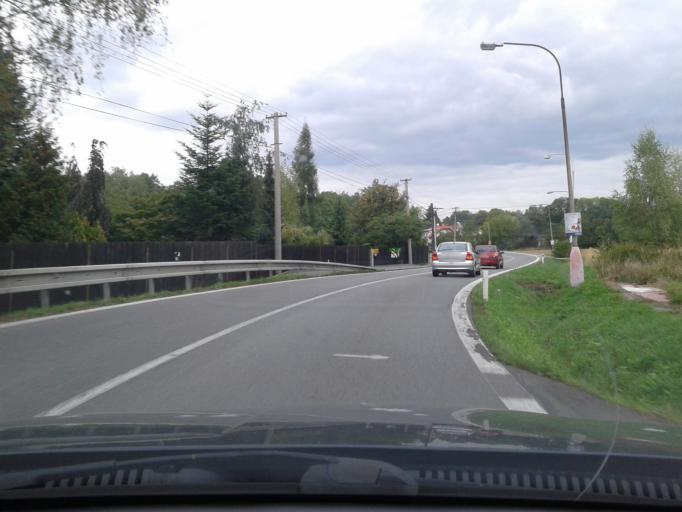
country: CZ
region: Moravskoslezsky
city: Orlova
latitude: 49.8696
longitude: 18.4426
